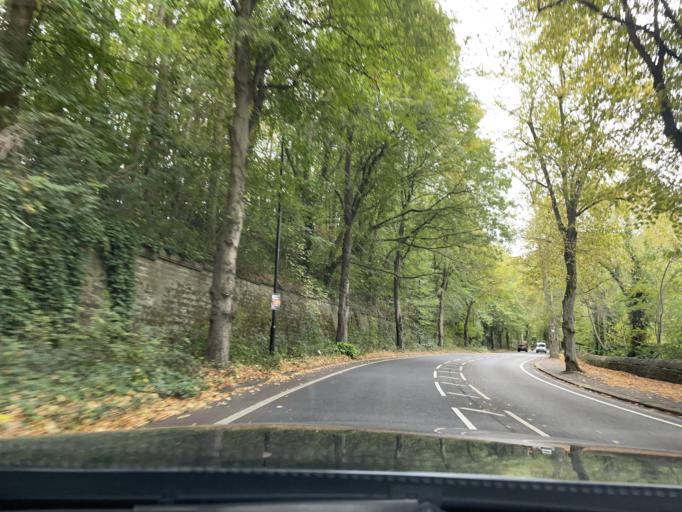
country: GB
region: England
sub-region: Sheffield
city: Sheffield
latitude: 53.3953
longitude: -1.5127
